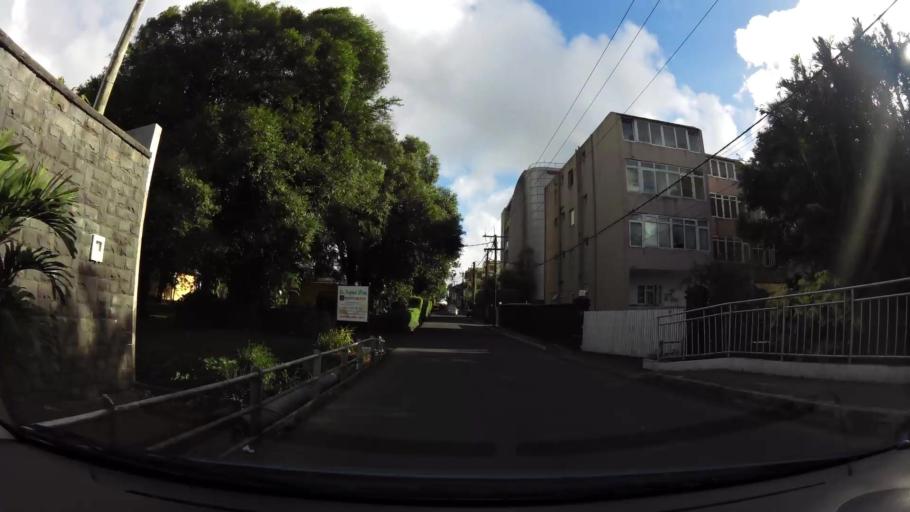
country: MU
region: Plaines Wilhems
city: Curepipe
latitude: -20.3191
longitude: 57.5176
